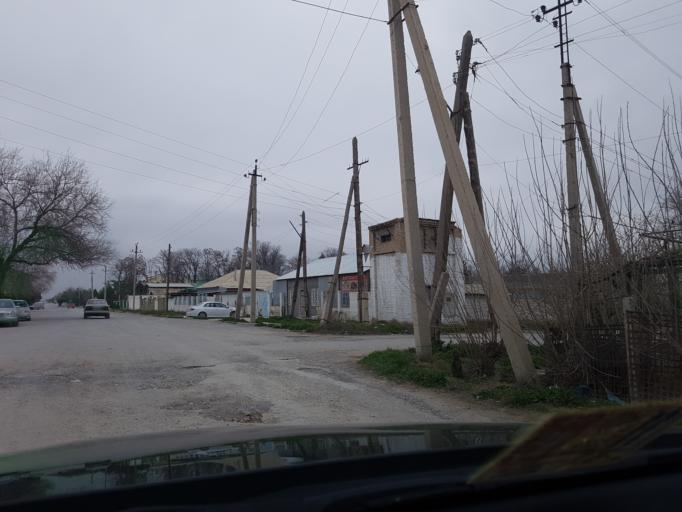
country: TM
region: Ahal
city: Abadan
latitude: 38.1552
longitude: 57.9653
